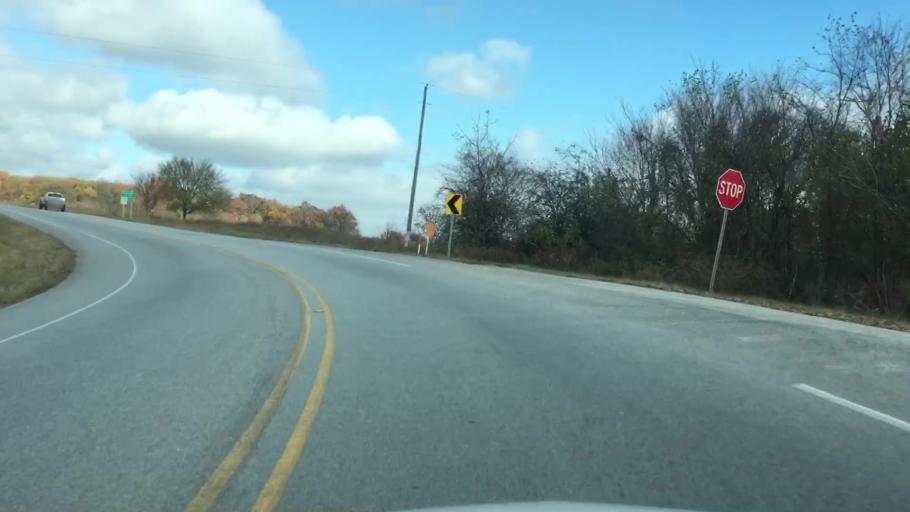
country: US
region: Arkansas
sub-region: Benton County
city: Centerton
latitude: 36.3007
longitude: -94.3041
